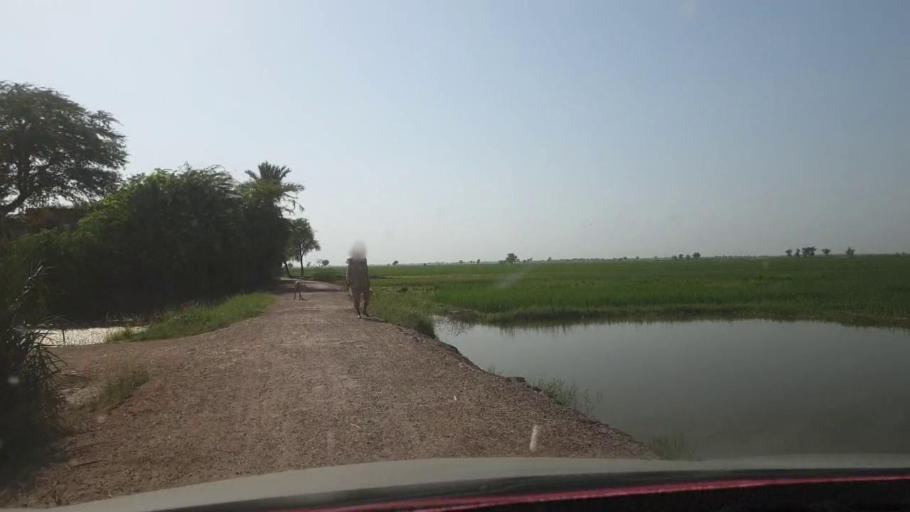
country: PK
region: Sindh
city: Nasirabad
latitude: 27.3853
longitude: 67.8666
